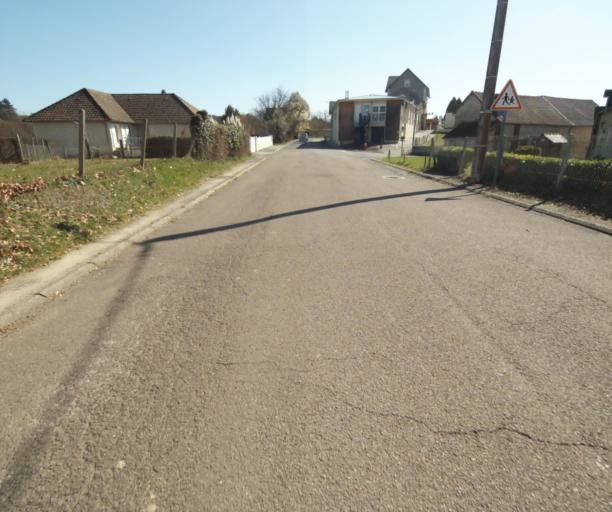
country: FR
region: Limousin
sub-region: Departement de la Correze
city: Saint-Mexant
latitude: 45.2865
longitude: 1.6581
